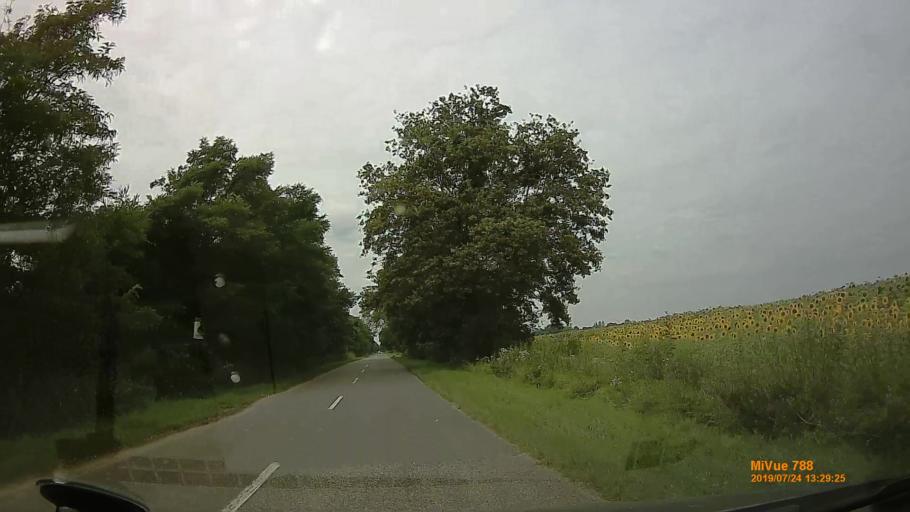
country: HU
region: Szabolcs-Szatmar-Bereg
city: Vasarosnameny
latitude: 48.2264
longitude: 22.3993
